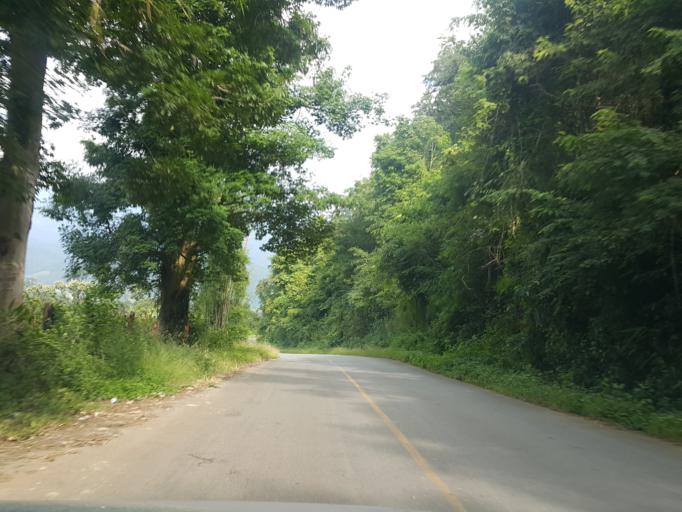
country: TH
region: Chiang Mai
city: Mae Chaem
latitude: 18.5490
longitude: 98.3893
